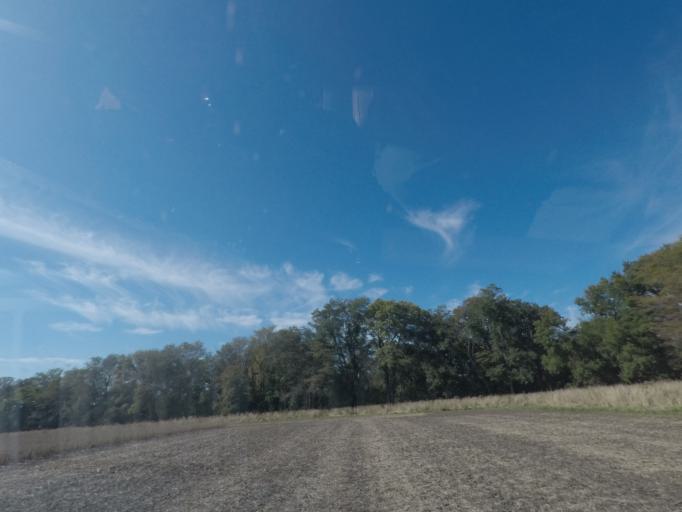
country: US
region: Iowa
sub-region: Story County
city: Nevada
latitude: 42.0312
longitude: -93.3758
